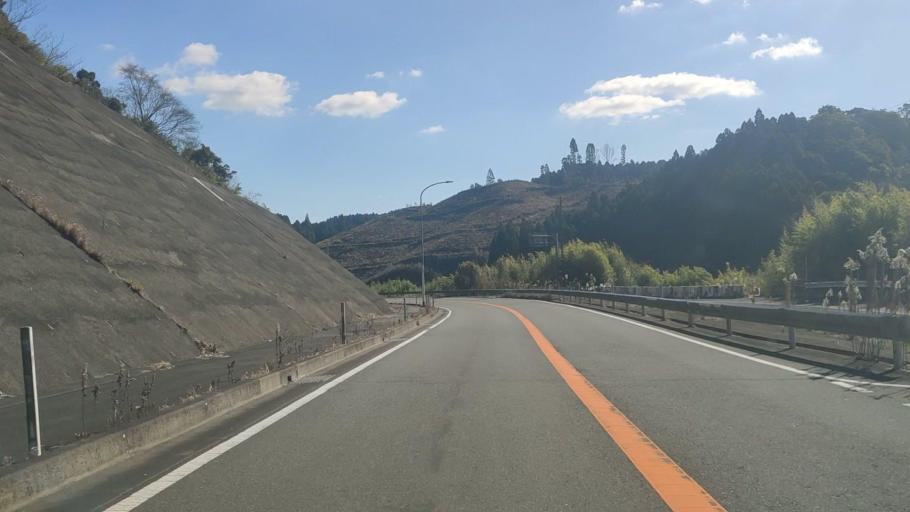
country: JP
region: Kagoshima
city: Sueyoshicho-ninokata
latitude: 31.6614
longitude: 130.8946
